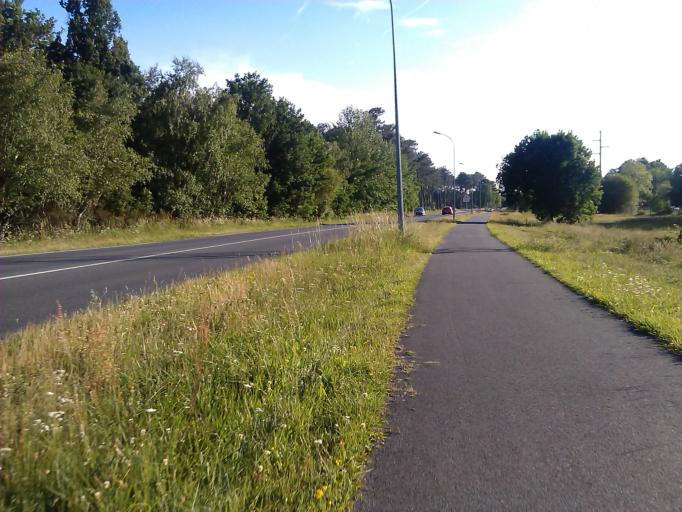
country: FR
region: Aquitaine
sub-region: Departement de la Gironde
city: Cestas
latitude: 44.7755
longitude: -0.6884
